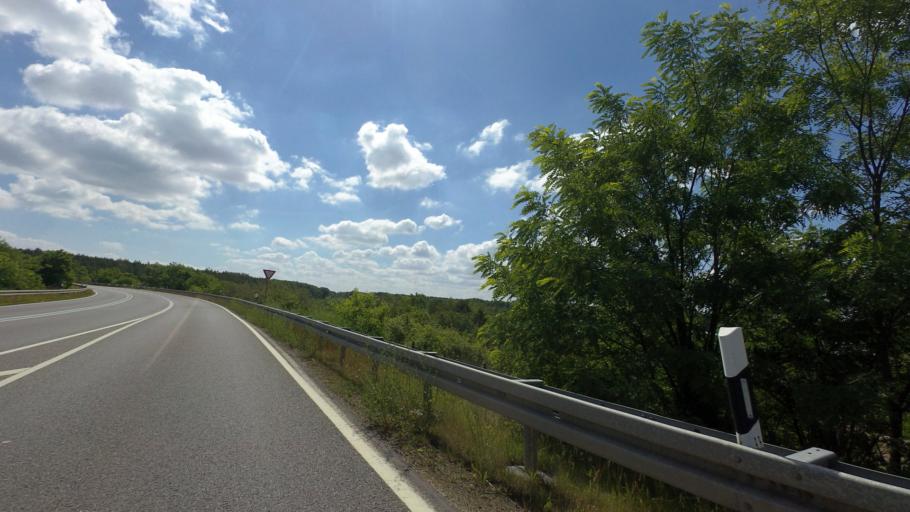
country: DE
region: Brandenburg
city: Senftenberg
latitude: 51.5297
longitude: 14.0175
